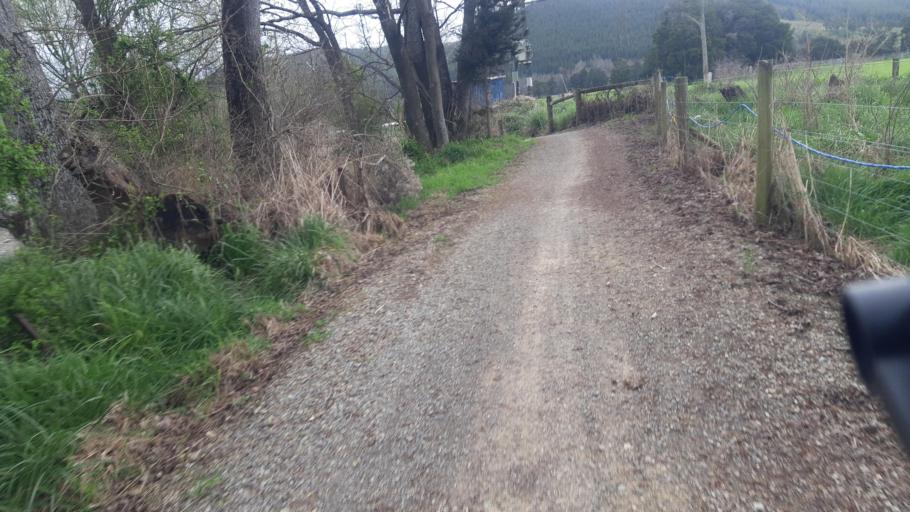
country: NZ
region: Tasman
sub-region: Tasman District
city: Wakefield
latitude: -41.4051
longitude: 173.0307
